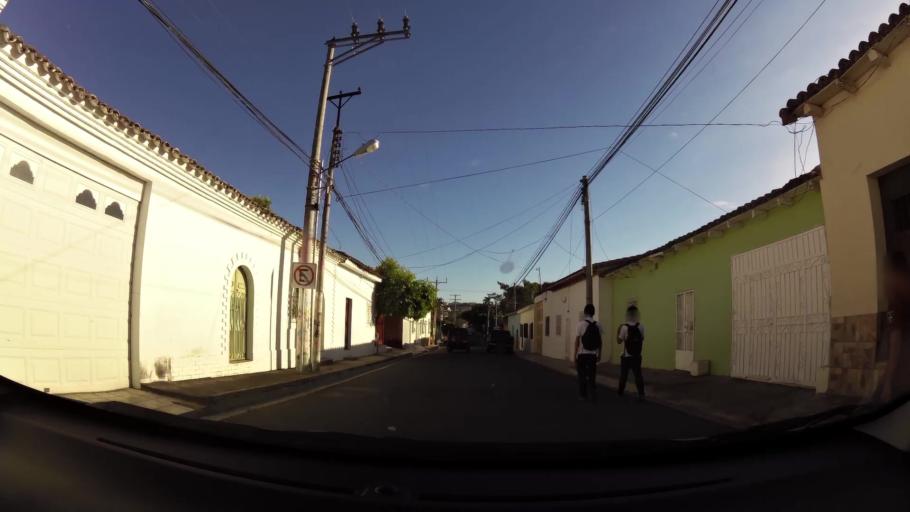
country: SV
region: Santa Ana
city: Metapan
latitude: 14.3350
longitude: -89.4481
